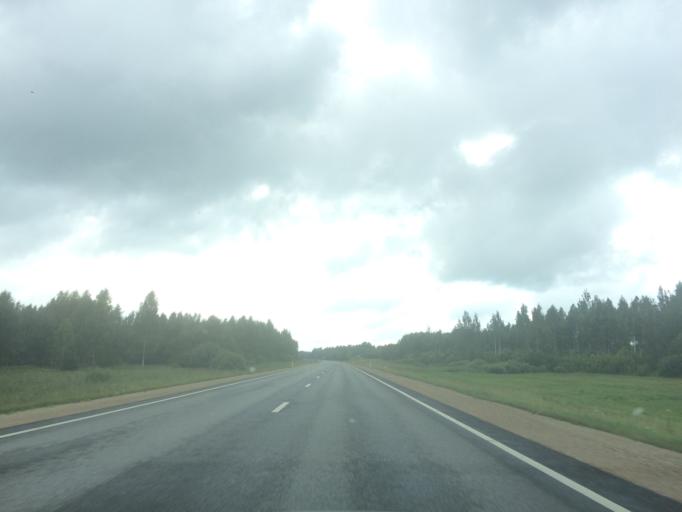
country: LV
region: Skriveri
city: Skriveri
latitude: 56.7556
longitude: 25.1139
